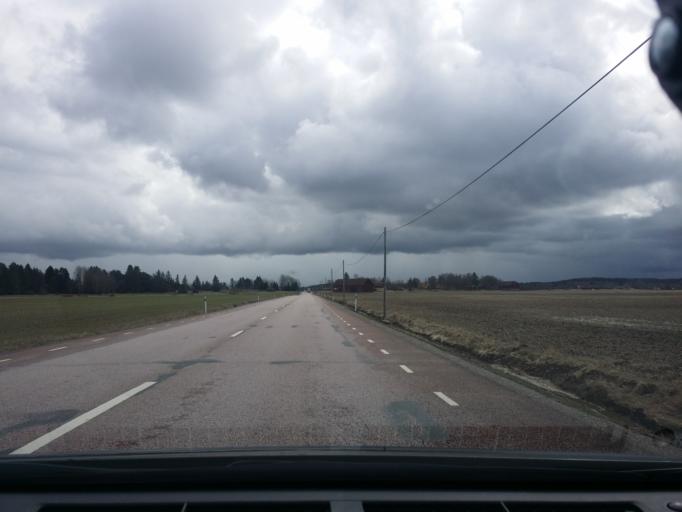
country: SE
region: Uppsala
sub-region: Enkopings Kommun
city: Irsta
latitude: 59.7814
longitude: 16.8456
